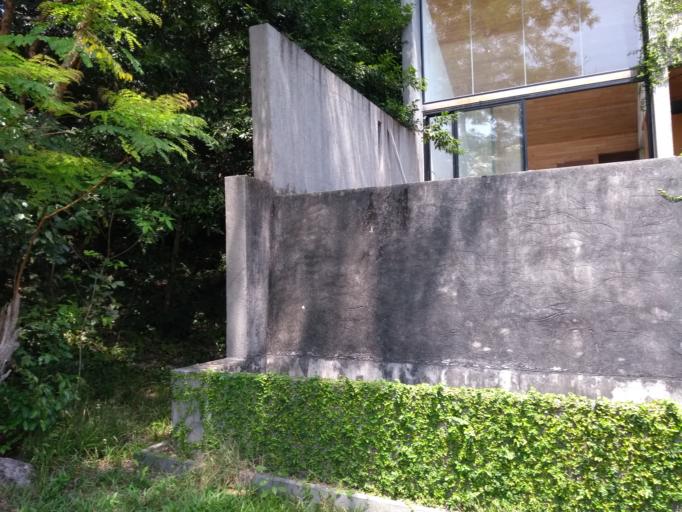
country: TH
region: Trat
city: Ko Chang Tai
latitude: 11.8327
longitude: 102.4602
